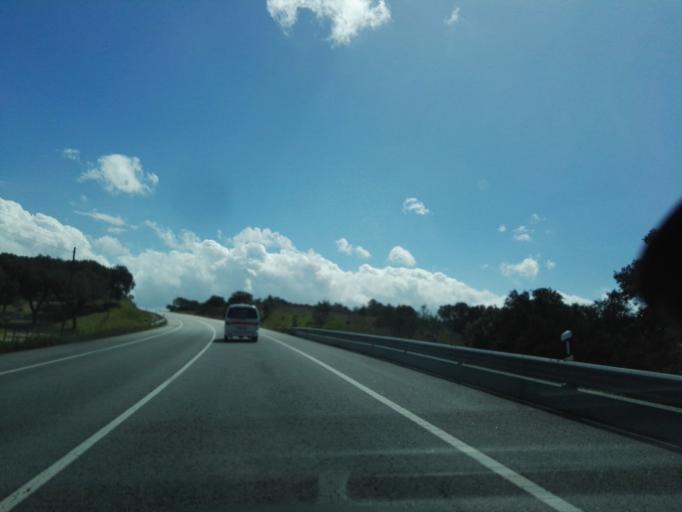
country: PT
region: Portalegre
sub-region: Portalegre
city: Alegrete
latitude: 39.1761
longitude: -7.3396
